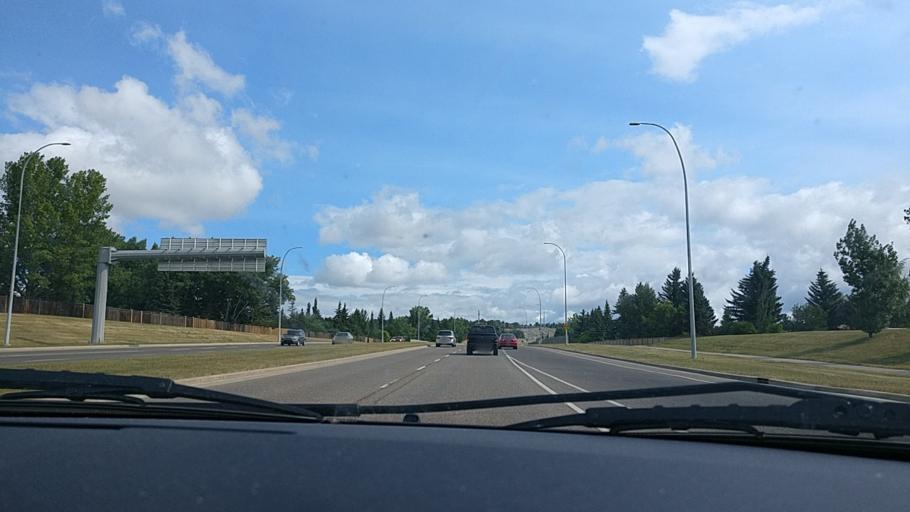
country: CA
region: Alberta
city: Calgary
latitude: 51.1128
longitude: -114.1762
